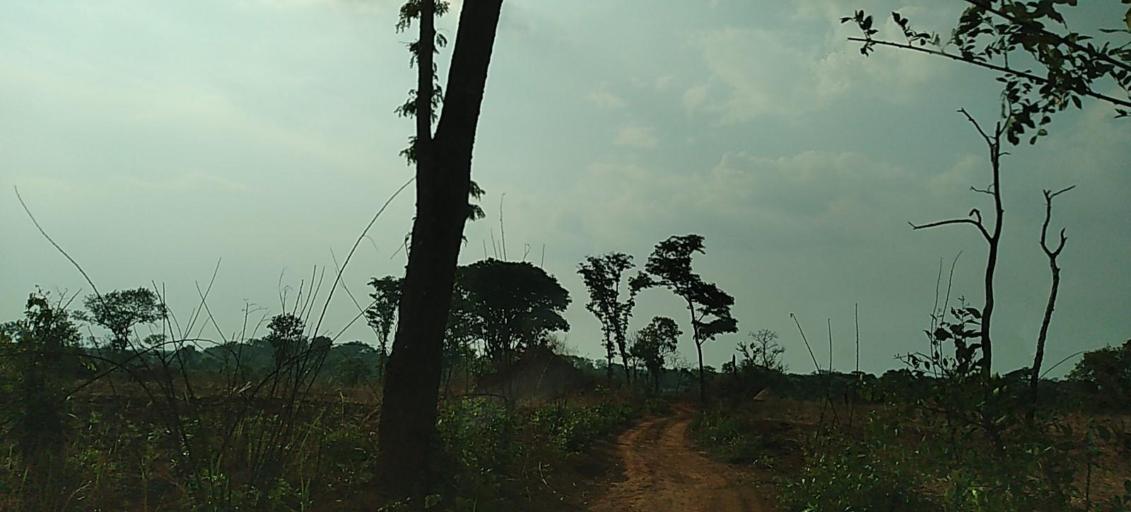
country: ZM
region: North-Western
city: Solwezi
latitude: -12.0572
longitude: 26.1598
